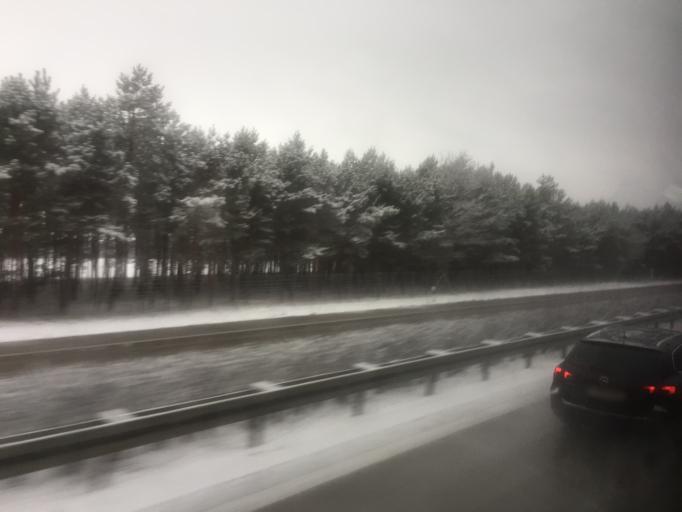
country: DE
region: Brandenburg
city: Kasel-Golzig
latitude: 52.0102
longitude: 13.7077
